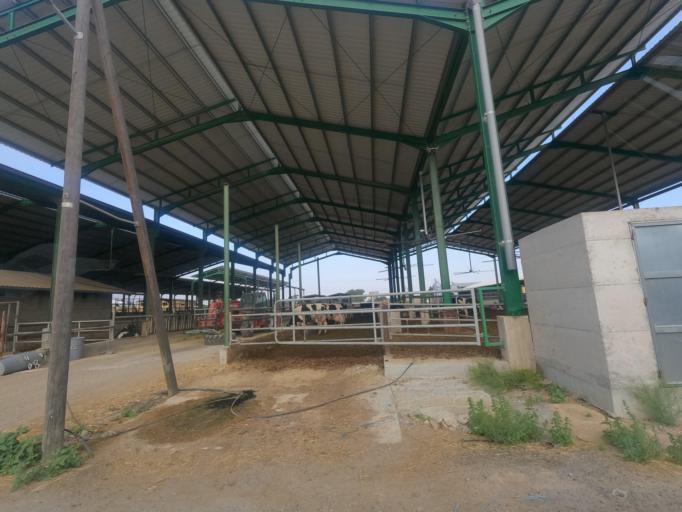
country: CY
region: Ammochostos
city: Achna
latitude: 35.0382
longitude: 33.7870
